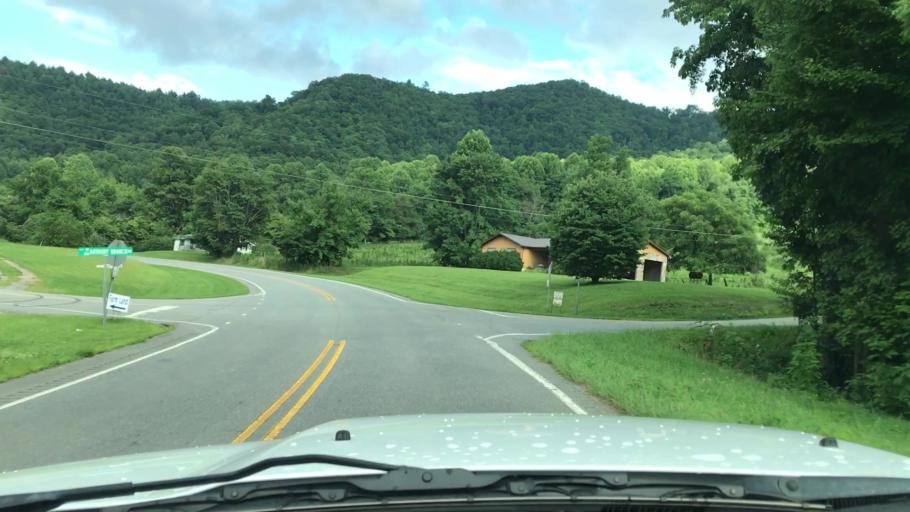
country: US
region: North Carolina
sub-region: Graham County
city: Robbinsville
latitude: 35.2700
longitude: -83.7530
